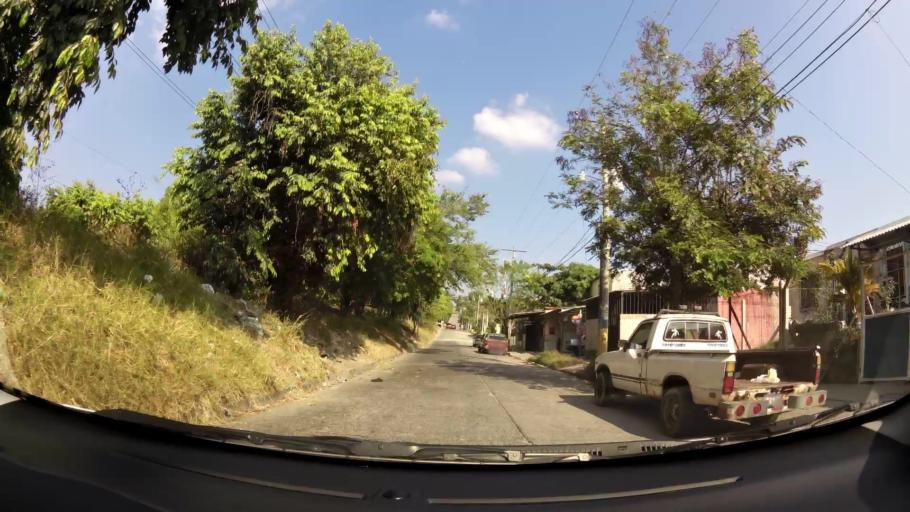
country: SV
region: San Salvador
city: Ilopango
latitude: 13.7258
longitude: -89.1105
